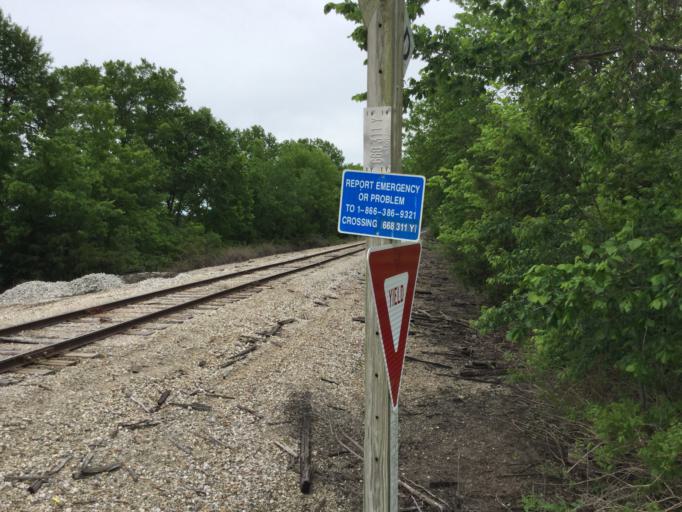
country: US
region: Kansas
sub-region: Labette County
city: Oswego
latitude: 37.1735
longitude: -95.1945
